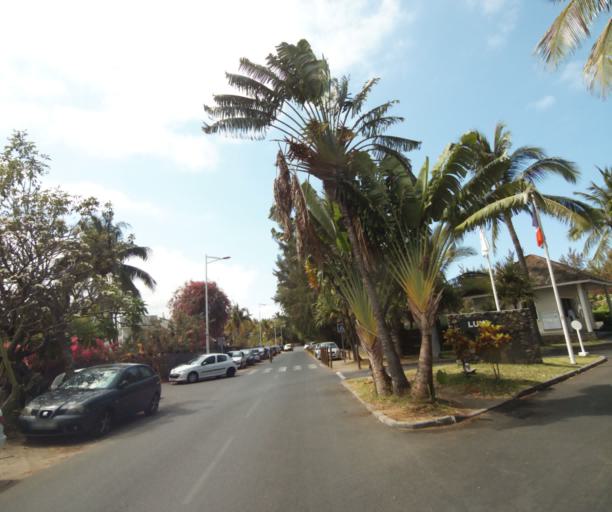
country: RE
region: Reunion
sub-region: Reunion
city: Trois-Bassins
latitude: -21.0872
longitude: 55.2302
